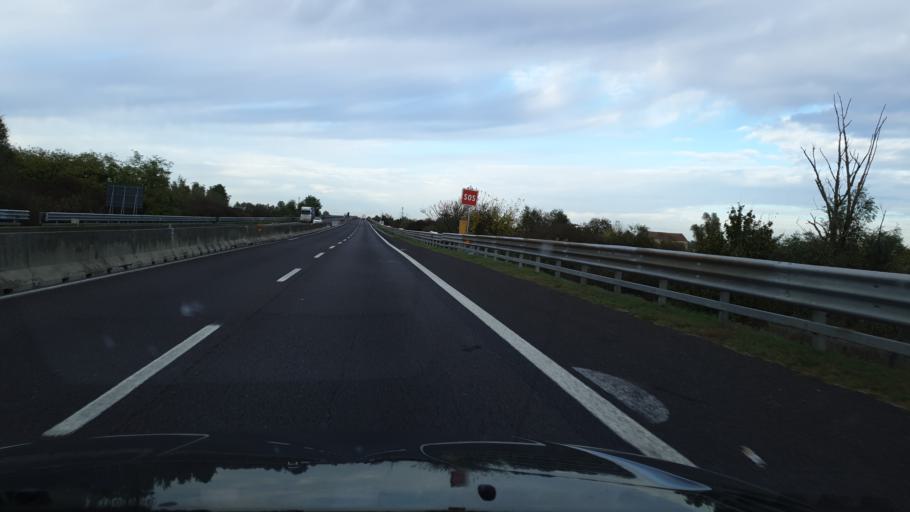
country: IT
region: Veneto
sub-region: Provincia di Padova
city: Boara Pisani
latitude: 45.0891
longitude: 11.7472
